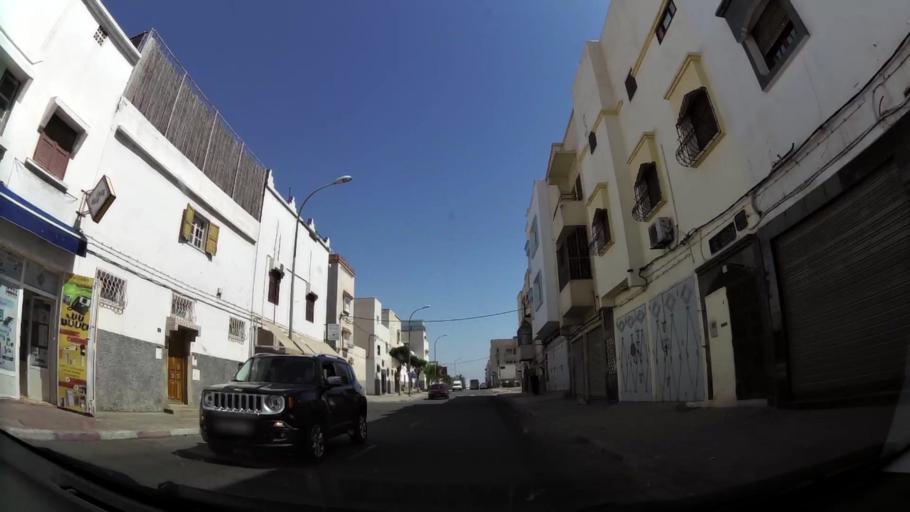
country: MA
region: Souss-Massa-Draa
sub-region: Agadir-Ida-ou-Tnan
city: Agadir
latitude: 30.4138
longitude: -9.5849
